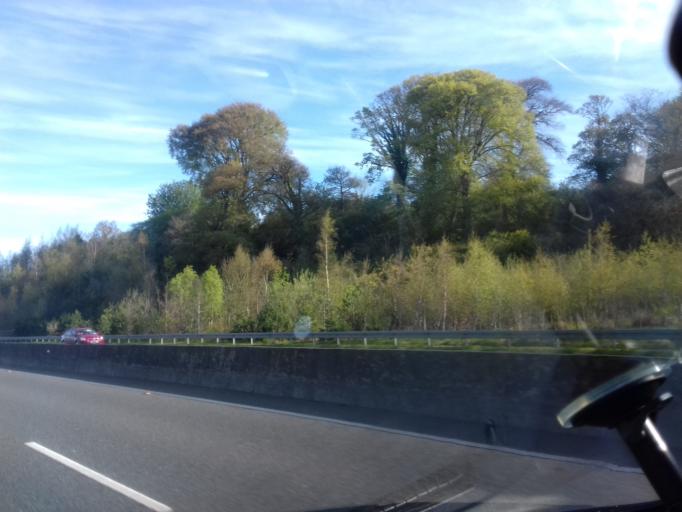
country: IE
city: Kentstown
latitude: 53.5917
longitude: -6.5837
